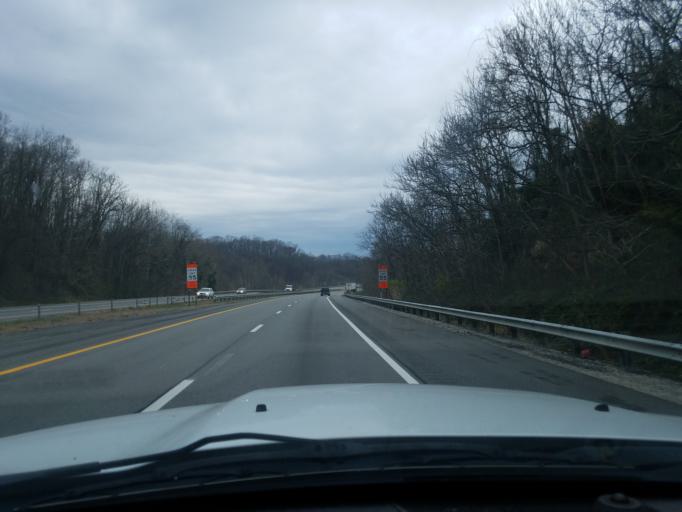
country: US
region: West Virginia
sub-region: Wayne County
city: Ceredo
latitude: 38.3905
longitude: -82.5629
